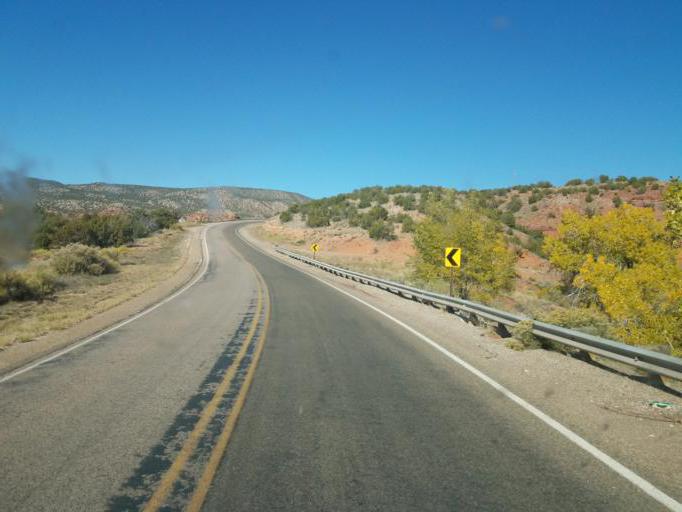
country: US
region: New Mexico
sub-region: Sandoval County
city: Jemez Pueblo
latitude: 35.6606
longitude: -106.7372
